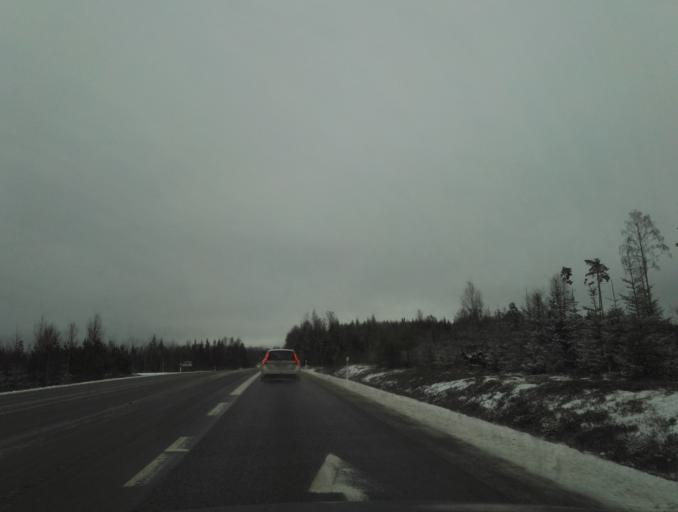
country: SE
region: Kronoberg
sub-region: Vaxjo Kommun
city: Gemla
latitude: 56.8287
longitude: 14.6937
